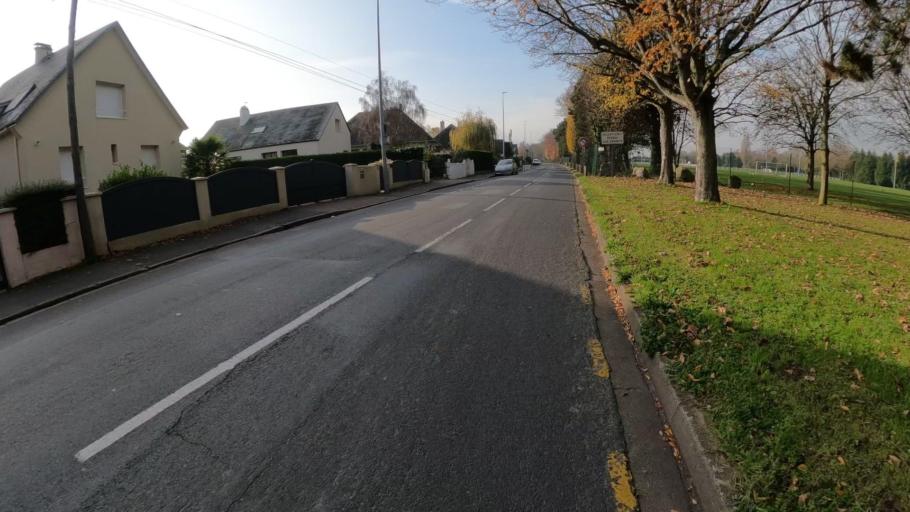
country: FR
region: Lower Normandy
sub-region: Departement du Calvados
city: Saint-Germain-la-Blanche-Herbe
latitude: 49.1937
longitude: -0.4030
